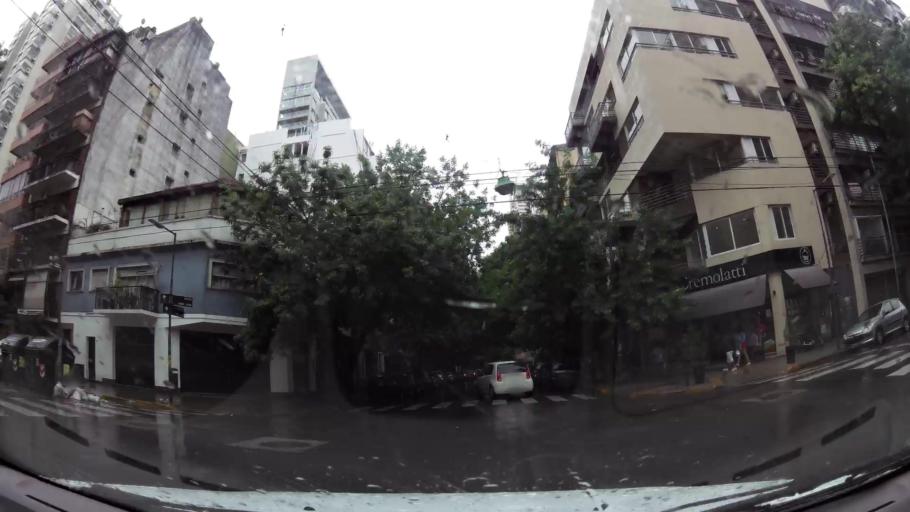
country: AR
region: Buenos Aires F.D.
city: Colegiales
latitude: -34.5778
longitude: -58.4244
